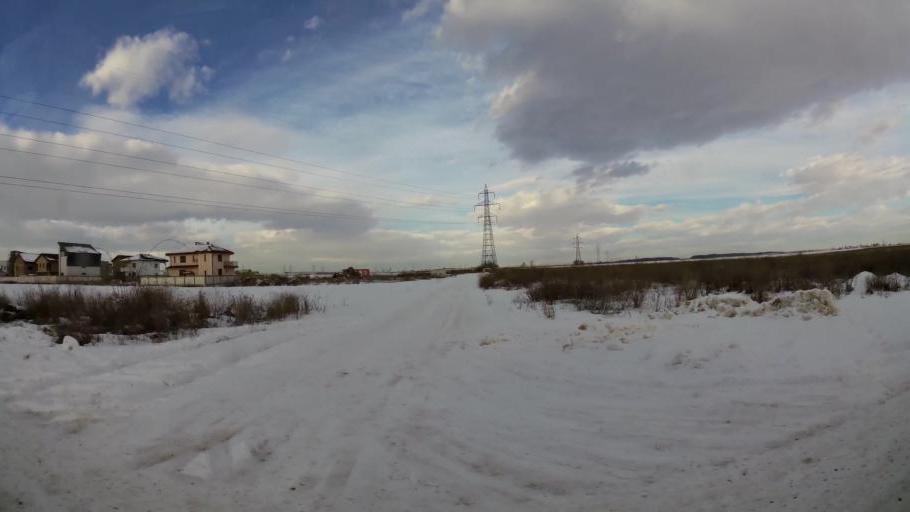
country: RO
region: Ilfov
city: Dobroesti
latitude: 44.4635
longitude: 26.1812
